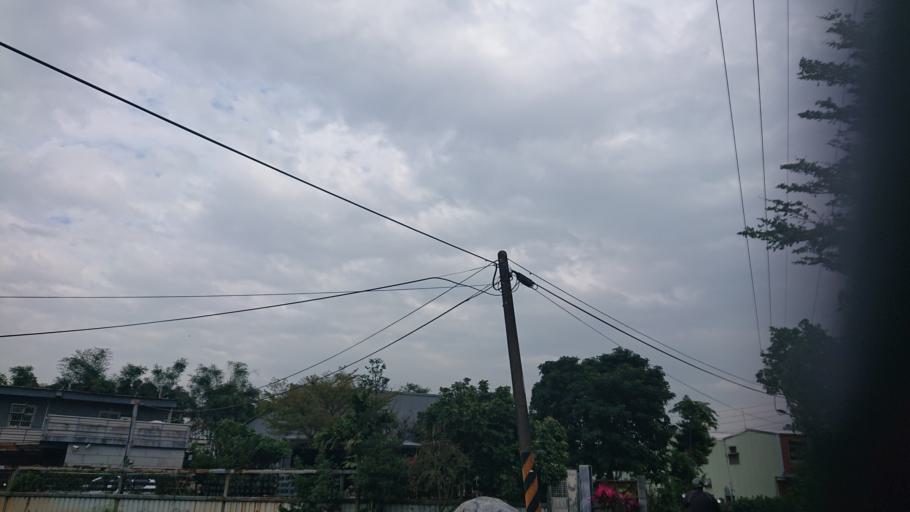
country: TW
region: Taiwan
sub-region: Taoyuan
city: Taoyuan
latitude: 24.9534
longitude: 121.3723
